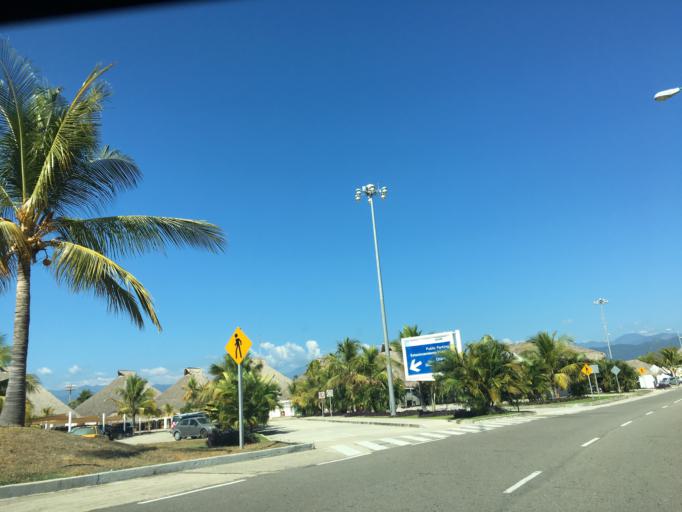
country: MX
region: Oaxaca
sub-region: Santa Maria Huatulco
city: Cuapinolito (Azulillo)
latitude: 15.7706
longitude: -96.2585
